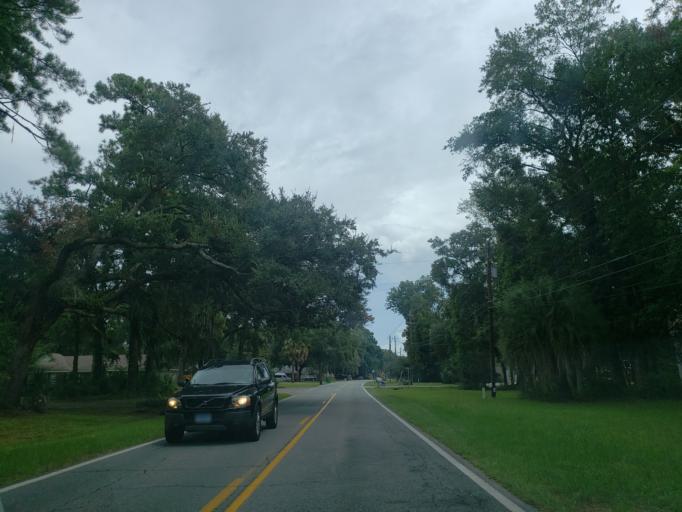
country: US
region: Georgia
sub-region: Chatham County
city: Wilmington Island
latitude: 32.0039
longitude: -80.9662
